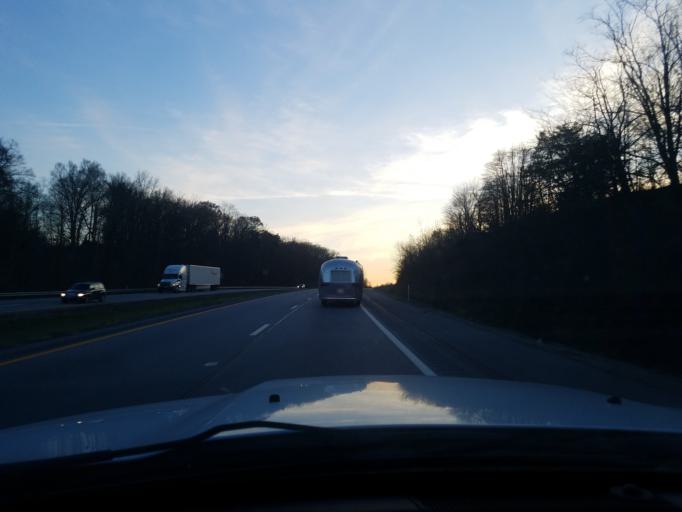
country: US
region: West Virginia
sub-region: Wood County
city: Williamstown
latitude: 39.3572
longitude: -81.4432
